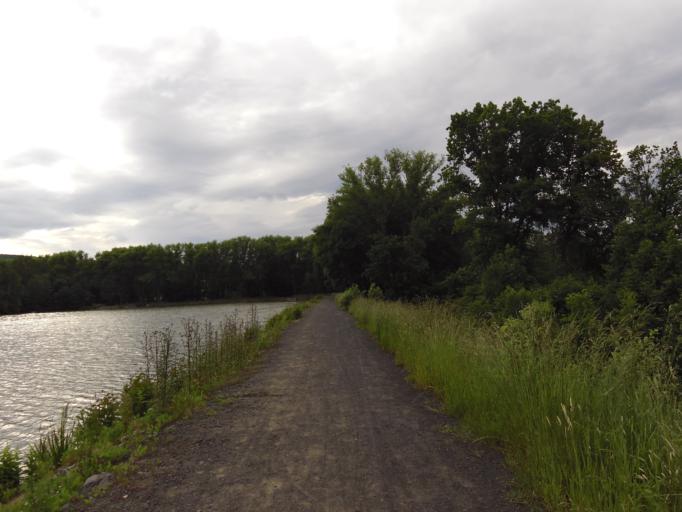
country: CZ
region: Ustecky
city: Varnsdorf
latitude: 50.8925
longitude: 14.6164
